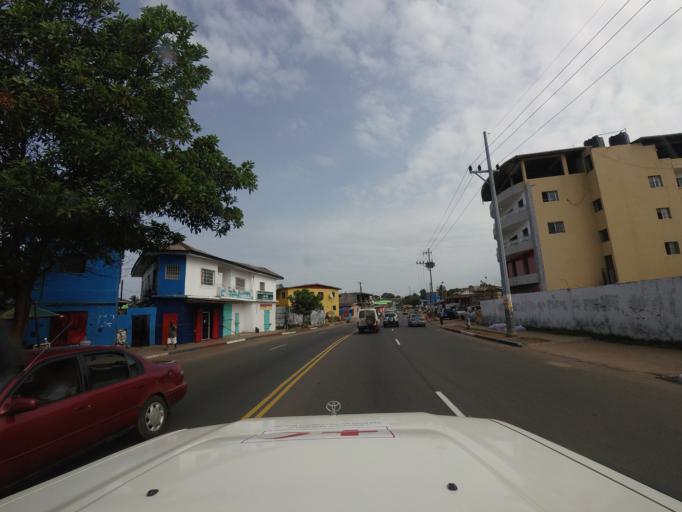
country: LR
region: Montserrado
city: Monrovia
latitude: 6.3090
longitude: -10.7984
